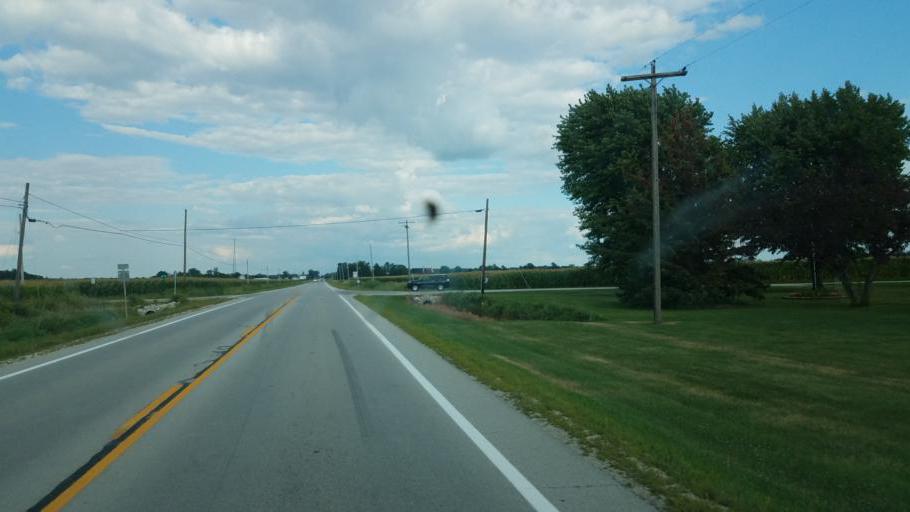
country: US
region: Ohio
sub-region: Sandusky County
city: Gibsonburg
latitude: 41.3412
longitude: -83.3605
